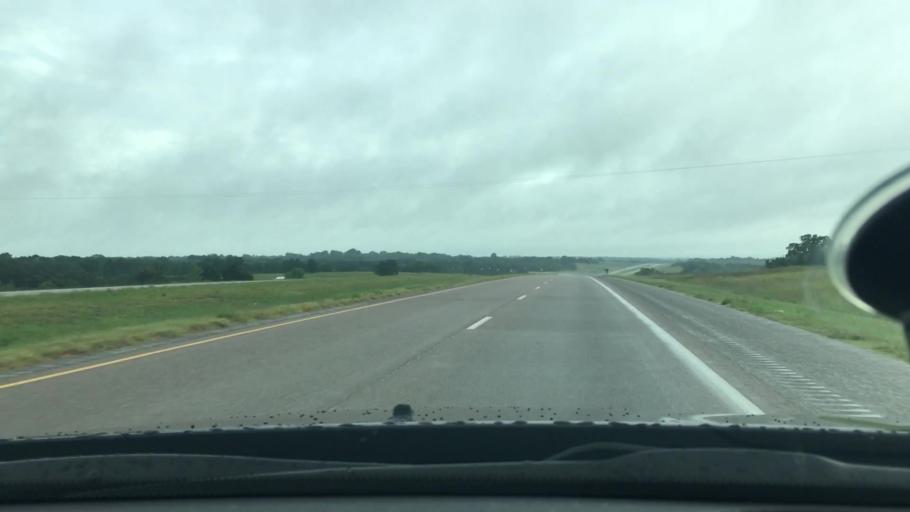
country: US
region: Oklahoma
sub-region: Pontotoc County
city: Byng
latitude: 34.8938
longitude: -96.6753
